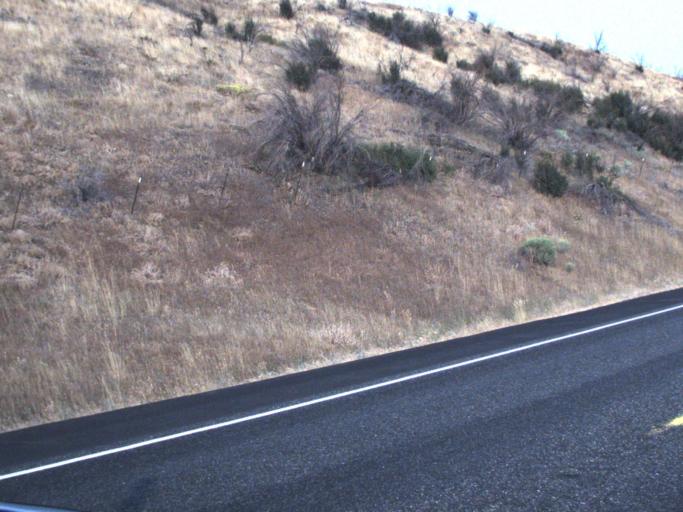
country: US
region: Washington
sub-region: Kittitas County
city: Ellensburg
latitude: 47.0812
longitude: -120.6393
